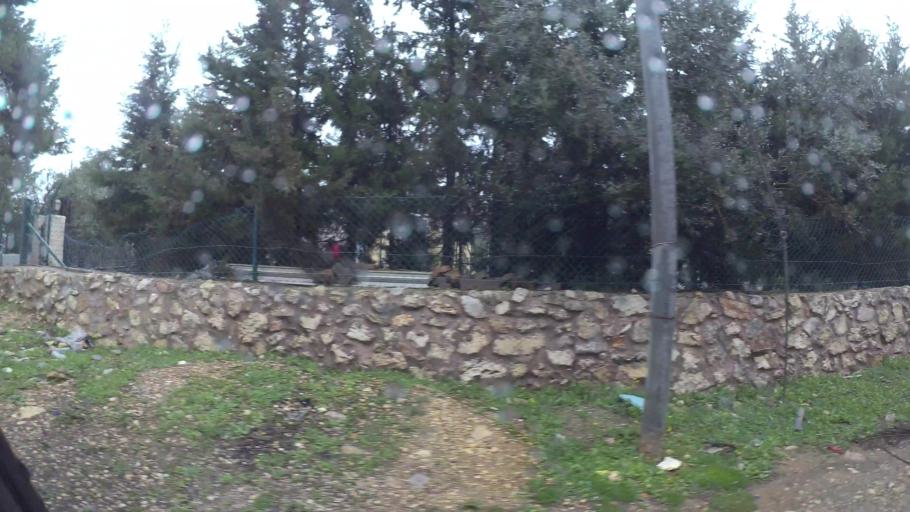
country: JO
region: Amman
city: Wadi as Sir
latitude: 32.0056
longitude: 35.7984
